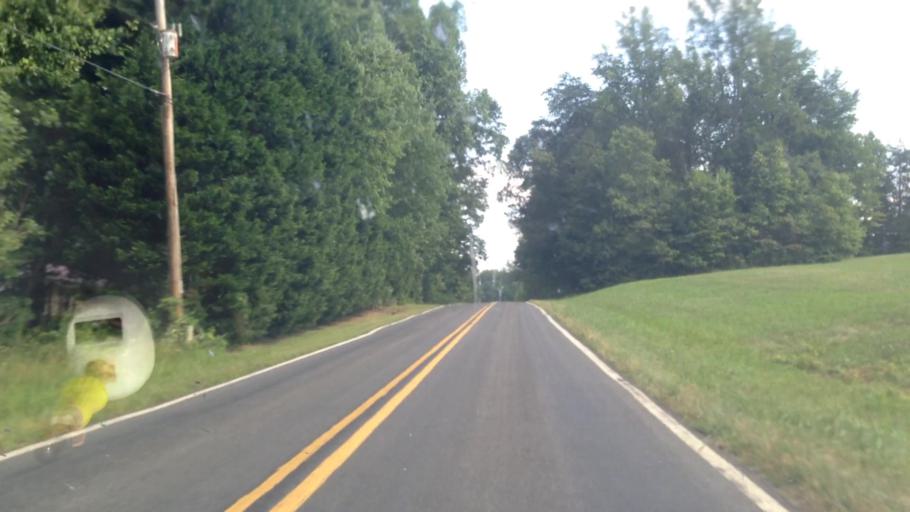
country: US
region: North Carolina
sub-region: Forsyth County
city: Walkertown
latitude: 36.2099
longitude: -80.1098
